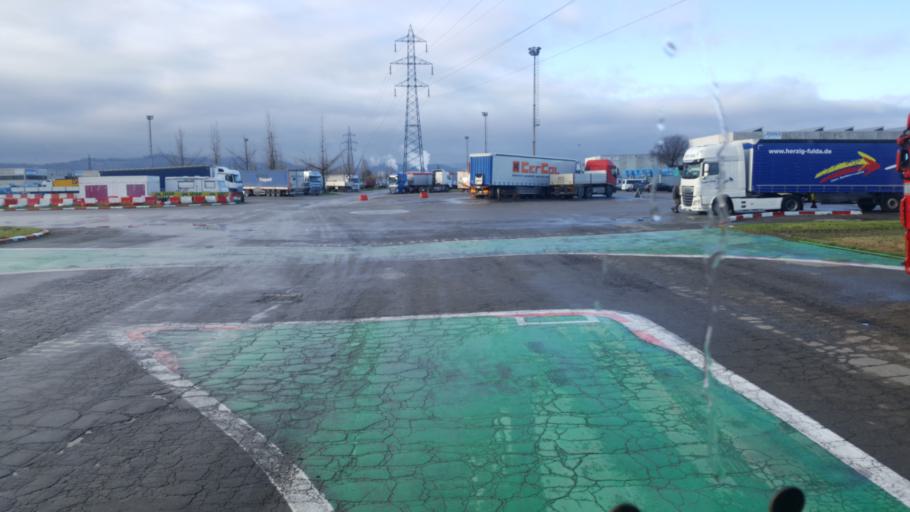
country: IT
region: Emilia-Romagna
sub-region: Provincia di Modena
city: Sassuolo
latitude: 44.5642
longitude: 10.7878
